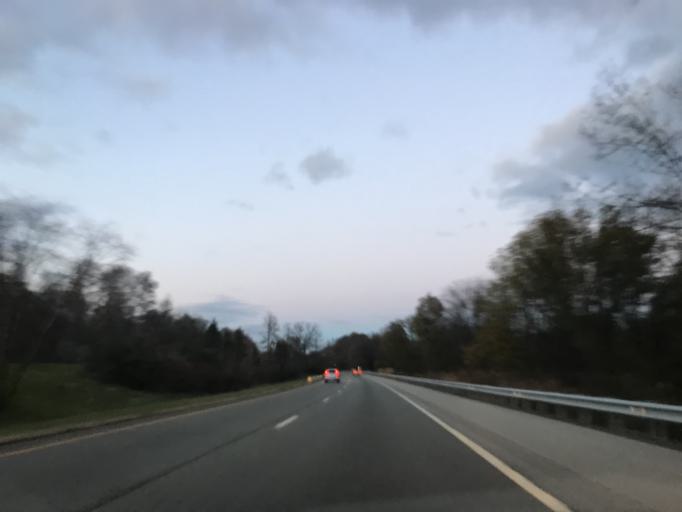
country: US
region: Delaware
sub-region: New Castle County
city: Bellefonte
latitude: 39.7908
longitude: -75.4915
